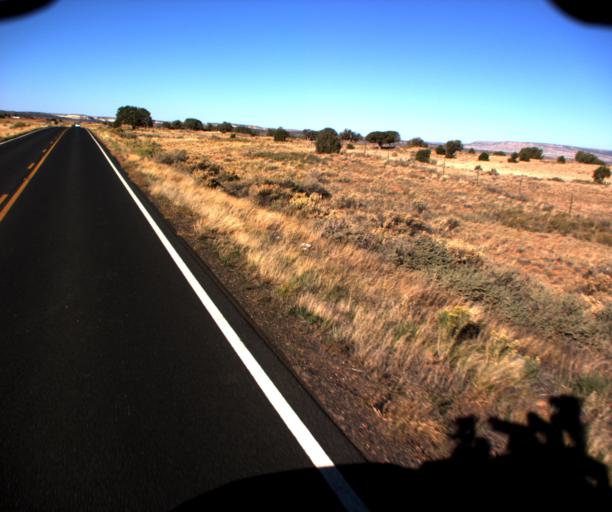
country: US
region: Arizona
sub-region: Apache County
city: Ganado
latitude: 35.7864
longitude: -109.6943
